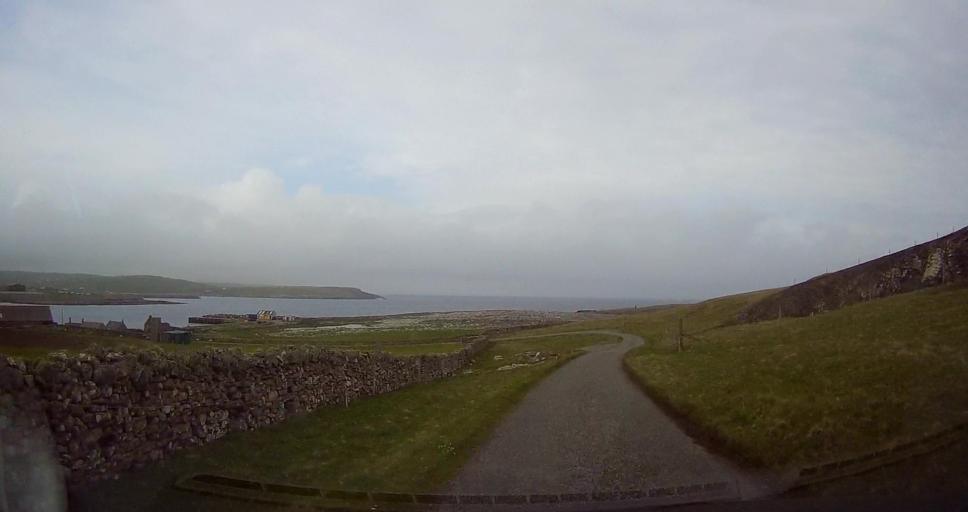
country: GB
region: Scotland
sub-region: Shetland Islands
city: Sandwick
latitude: 59.8707
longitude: -1.2779
